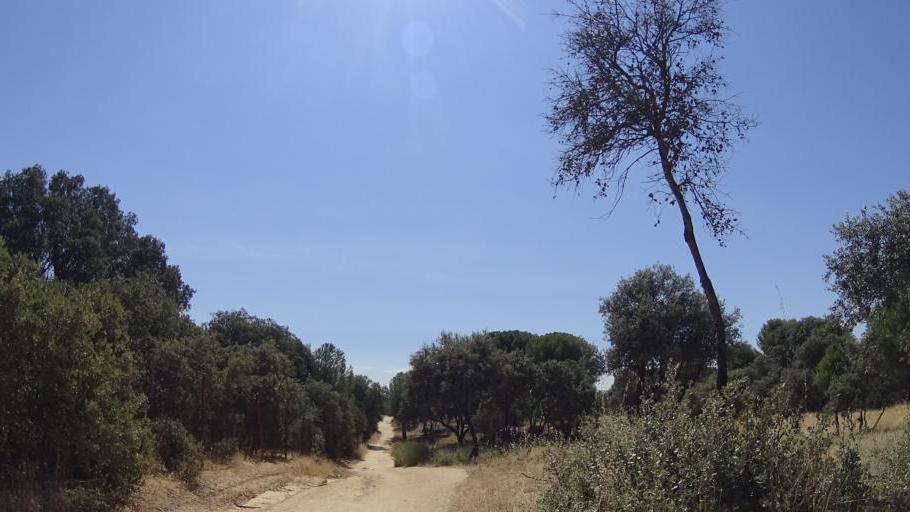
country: ES
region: Madrid
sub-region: Provincia de Madrid
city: Majadahonda
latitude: 40.4418
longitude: -3.8641
